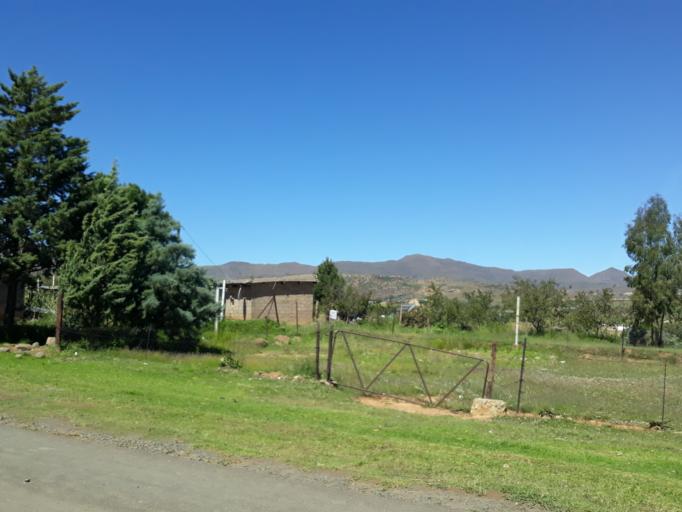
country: LS
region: Mohale's Hoek District
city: Mohale's Hoek
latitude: -30.1082
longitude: 27.4715
